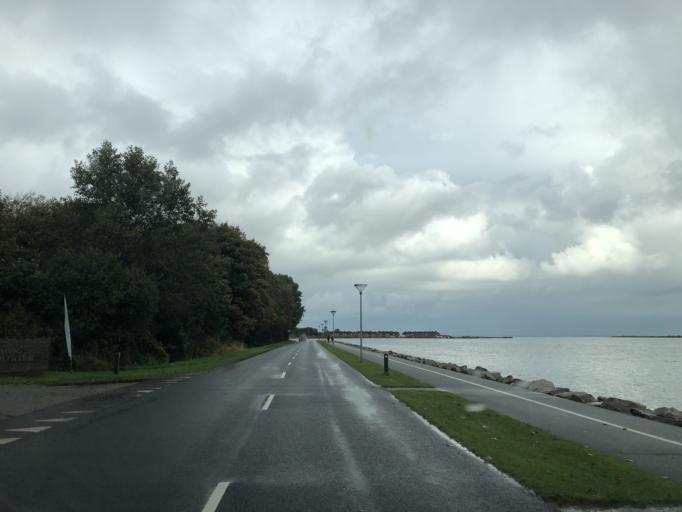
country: DK
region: Central Jutland
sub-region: Lemvig Kommune
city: Lemvig
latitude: 56.5575
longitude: 8.2954
